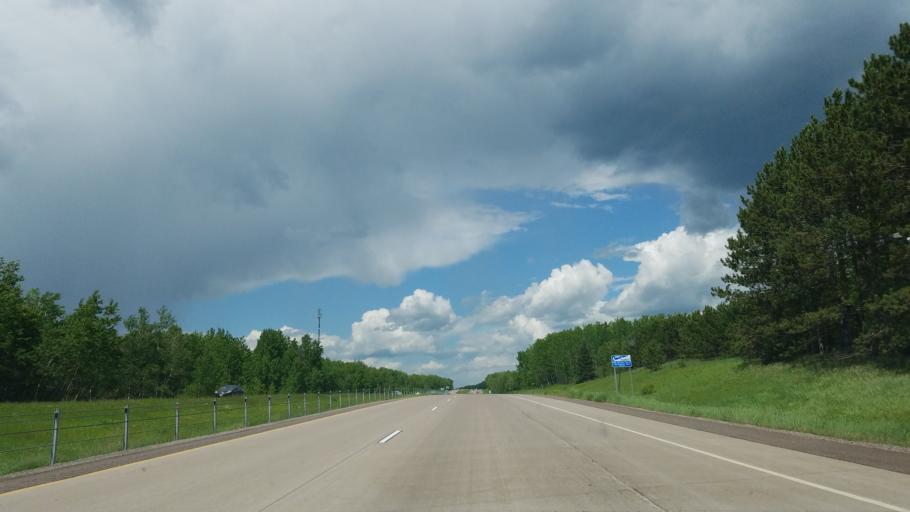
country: US
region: Minnesota
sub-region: Carlton County
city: Moose Lake
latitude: 46.4539
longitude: -92.7290
